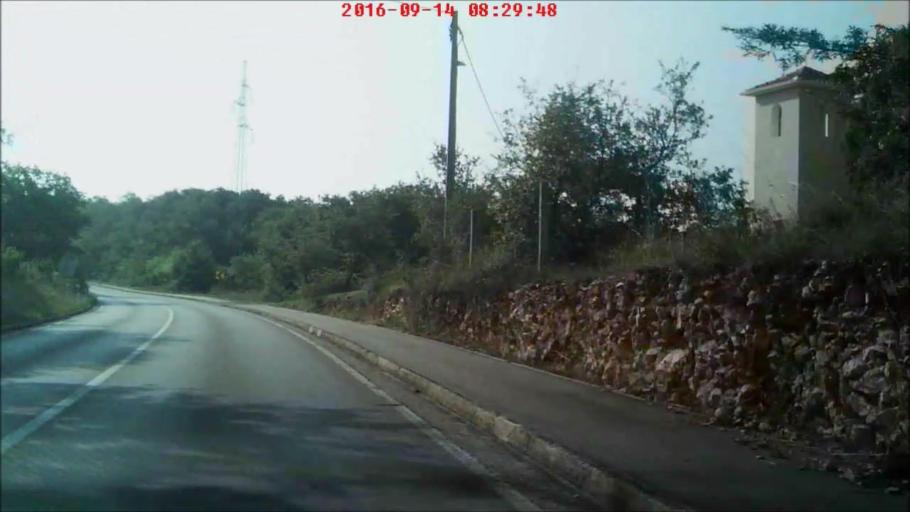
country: HR
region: Zadarska
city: Zadar
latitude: 44.1778
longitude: 15.2867
